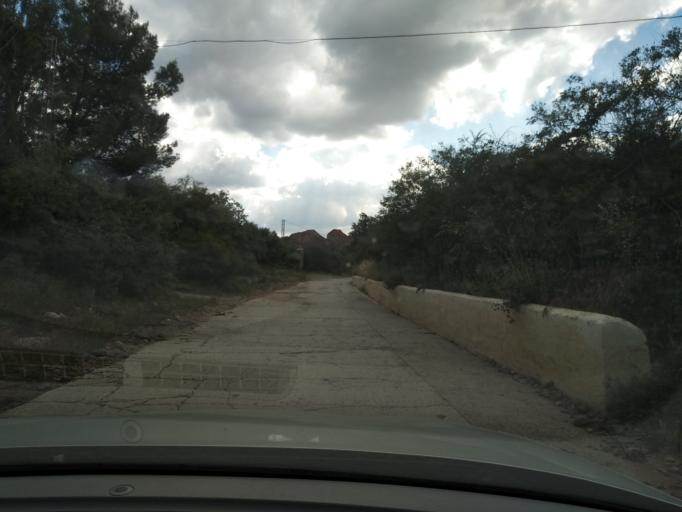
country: ES
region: Andalusia
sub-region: Provincia de Granada
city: Marchal
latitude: 37.2948
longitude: -3.2005
